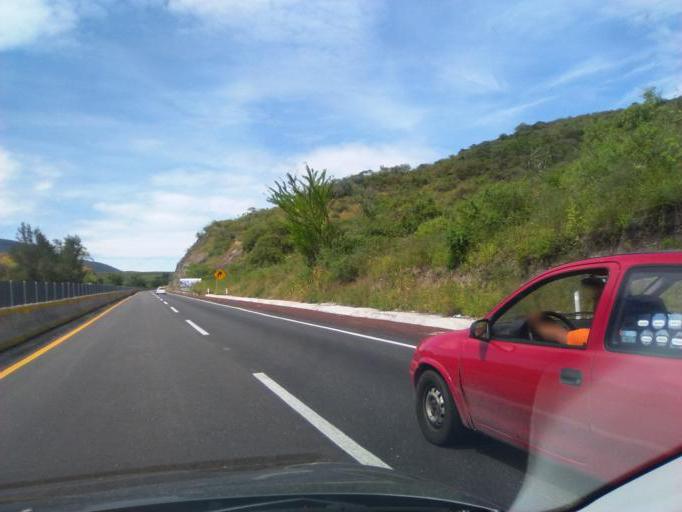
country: MX
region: Guerrero
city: Mazatlan
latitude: 17.4067
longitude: -99.4626
